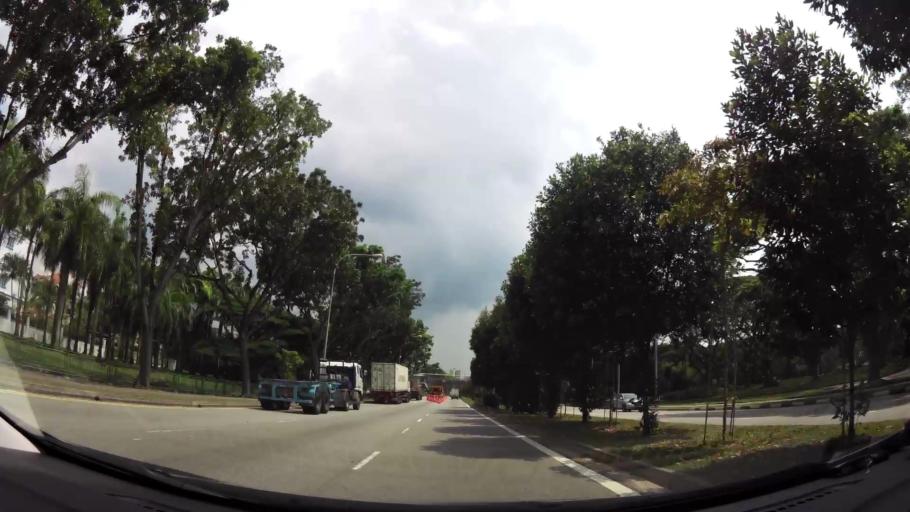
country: SG
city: Singapore
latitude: 1.2899
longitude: 103.7718
